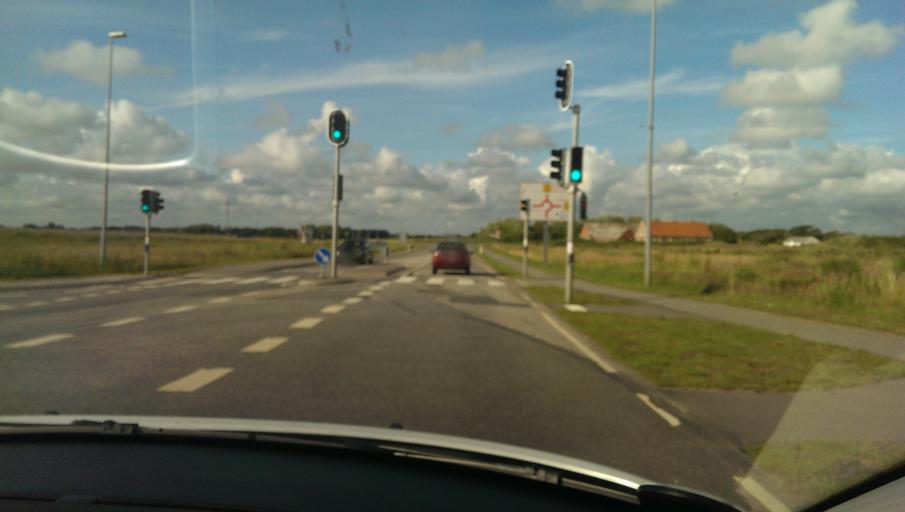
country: DK
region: Central Jutland
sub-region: Ringkobing-Skjern Kommune
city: Ringkobing
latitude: 56.1042
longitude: 8.2581
